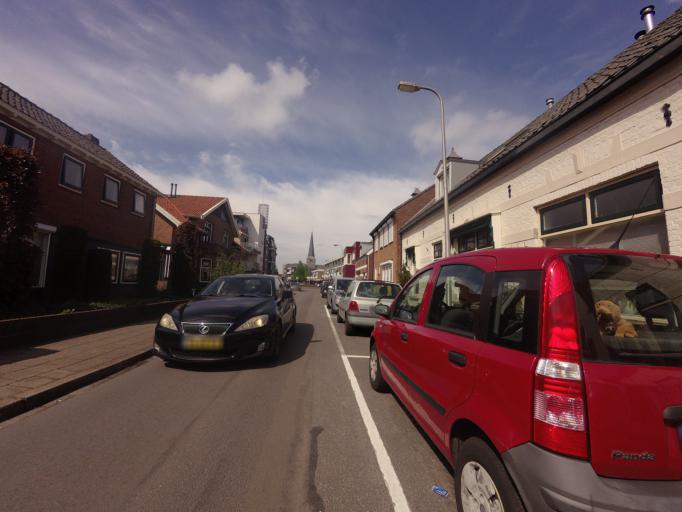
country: NL
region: Overijssel
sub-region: Gemeente Haaksbergen
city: Haaksbergen
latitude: 52.1524
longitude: 6.7413
